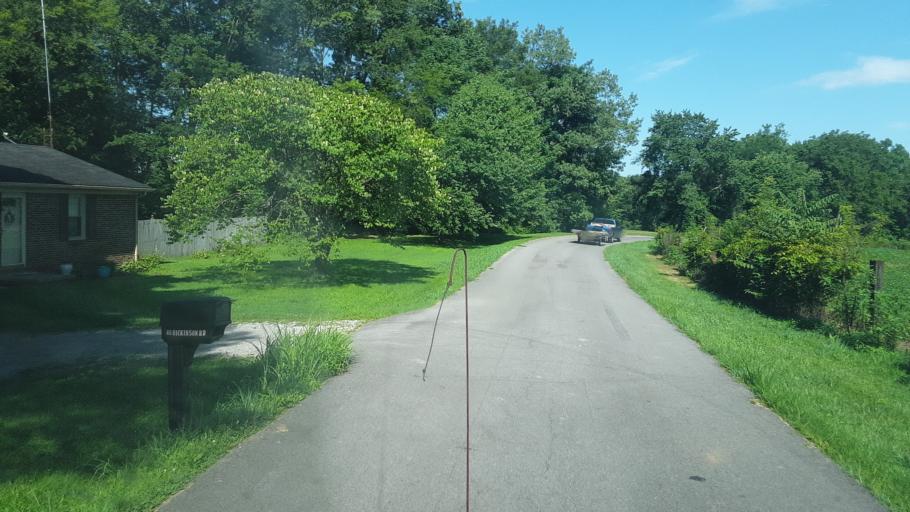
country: US
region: Kentucky
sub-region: Todd County
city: Elkton
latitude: 36.7525
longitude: -87.2237
